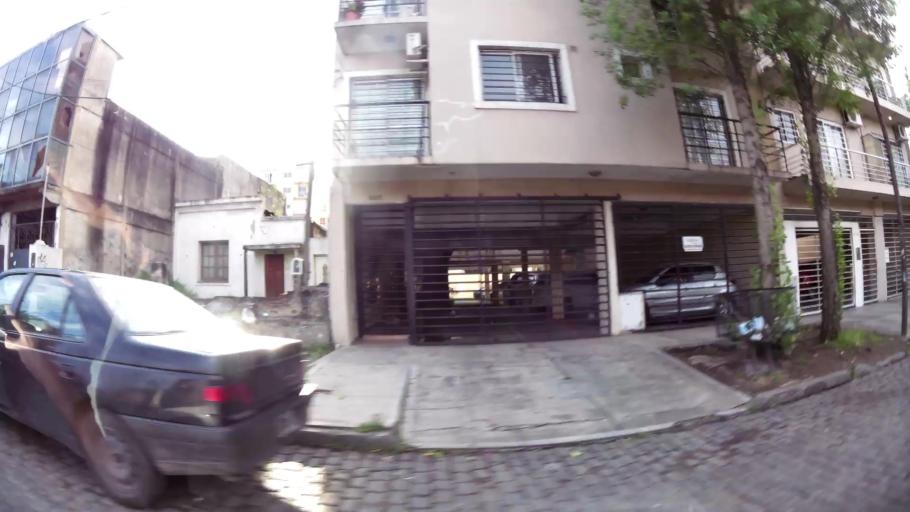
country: AR
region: Buenos Aires
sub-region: Partido de Moron
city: Moron
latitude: -34.6574
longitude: -58.6187
